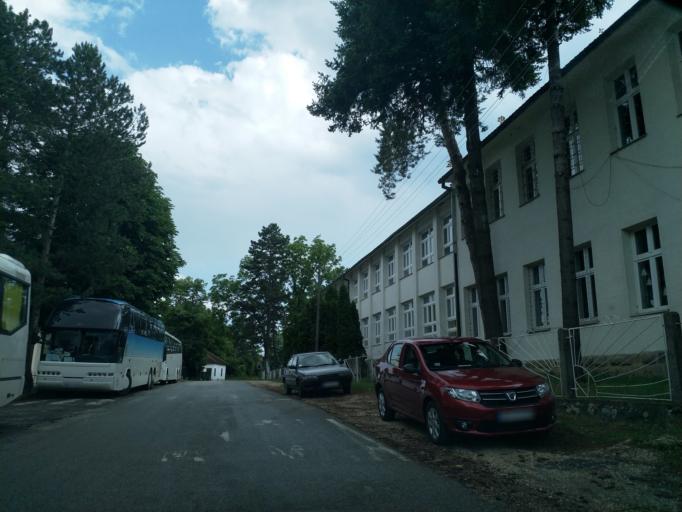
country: RS
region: Central Serbia
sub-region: Borski Okrug
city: Bor
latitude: 44.0095
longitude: 21.9849
